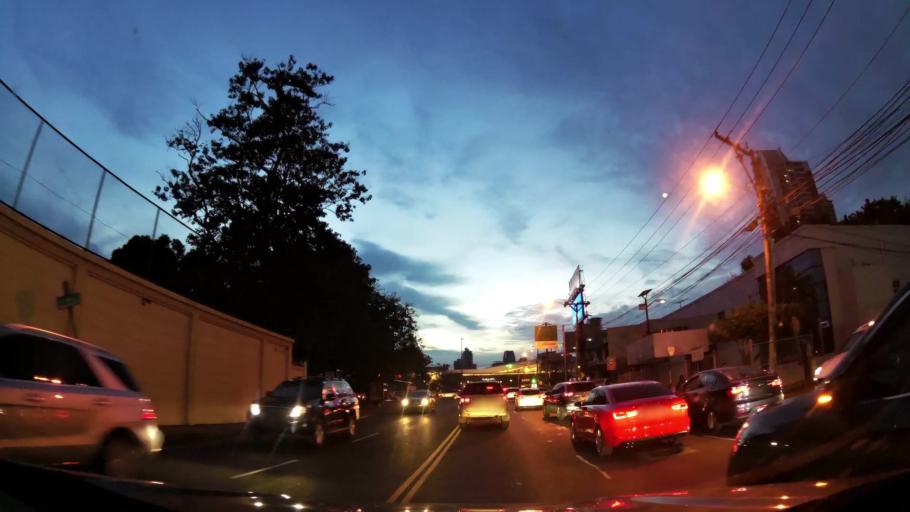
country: PA
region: Panama
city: Panama
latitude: 8.9871
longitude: -79.5088
